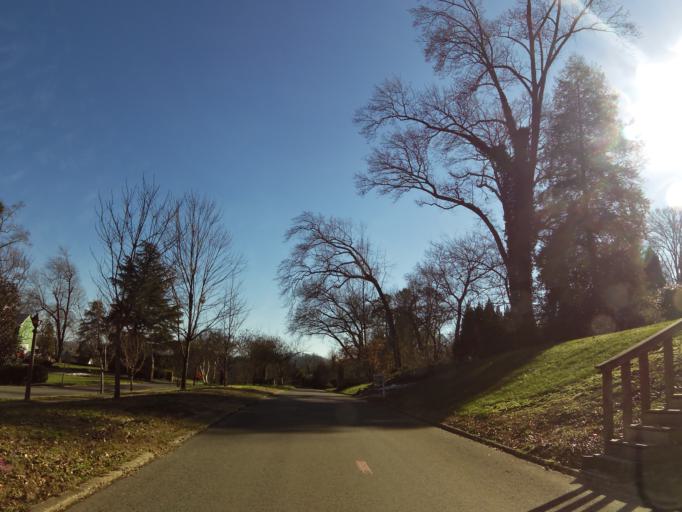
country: US
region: Tennessee
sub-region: Knox County
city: Knoxville
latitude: 35.9389
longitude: -83.9581
